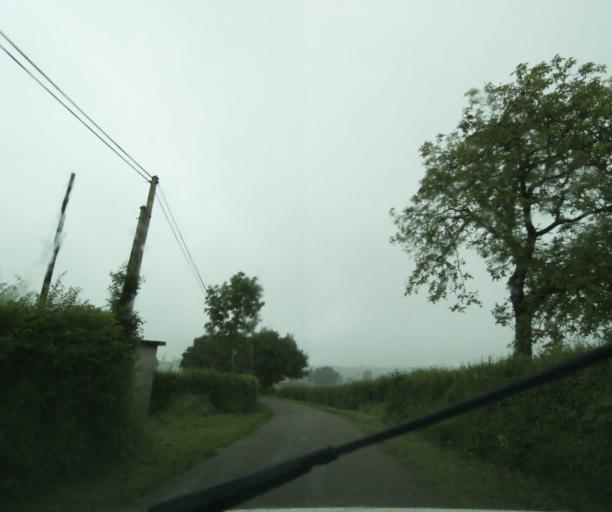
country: FR
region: Bourgogne
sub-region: Departement de Saone-et-Loire
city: Charolles
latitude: 46.4262
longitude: 4.3479
